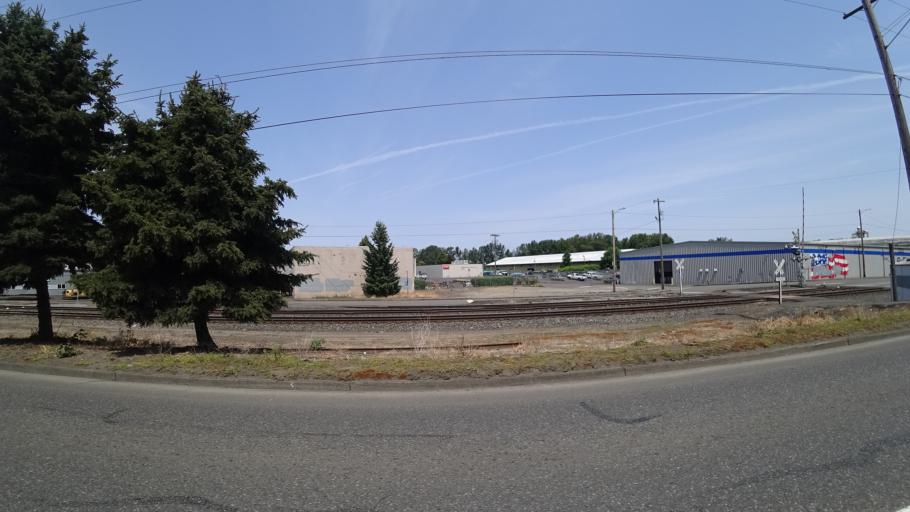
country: US
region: Washington
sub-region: Clark County
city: Vancouver
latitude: 45.5876
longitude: -122.6939
